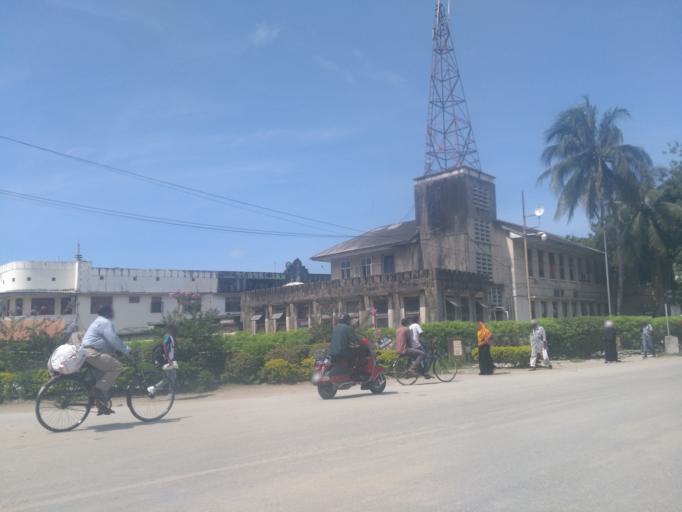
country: TZ
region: Zanzibar Urban/West
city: Zanzibar
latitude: -6.1580
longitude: 39.1954
